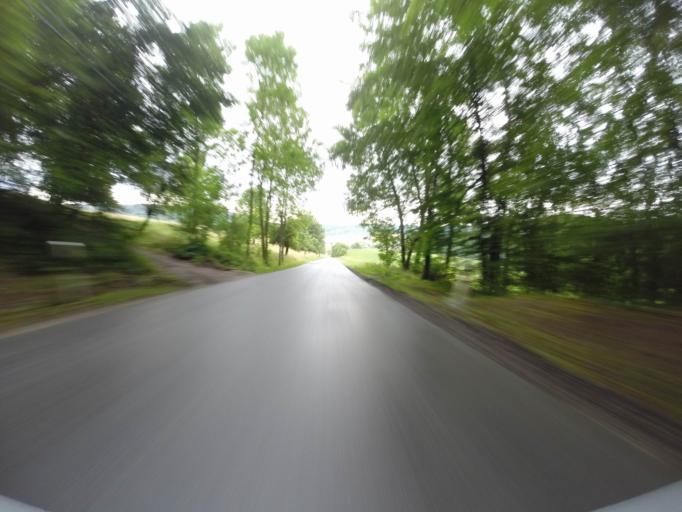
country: DE
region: Thuringia
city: Grosslobichau
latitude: 50.9392
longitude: 11.6887
